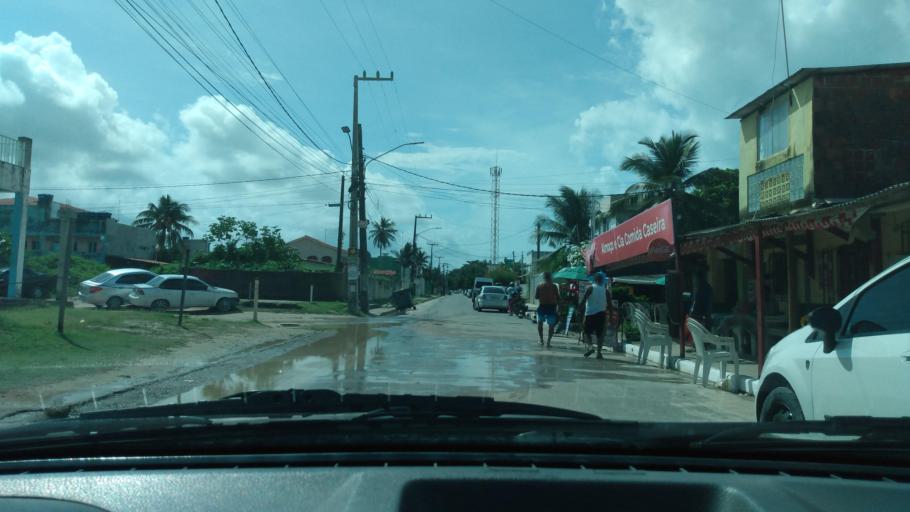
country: BR
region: Pernambuco
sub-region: Cabo De Santo Agostinho
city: Cabo
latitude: -8.3367
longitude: -34.9514
